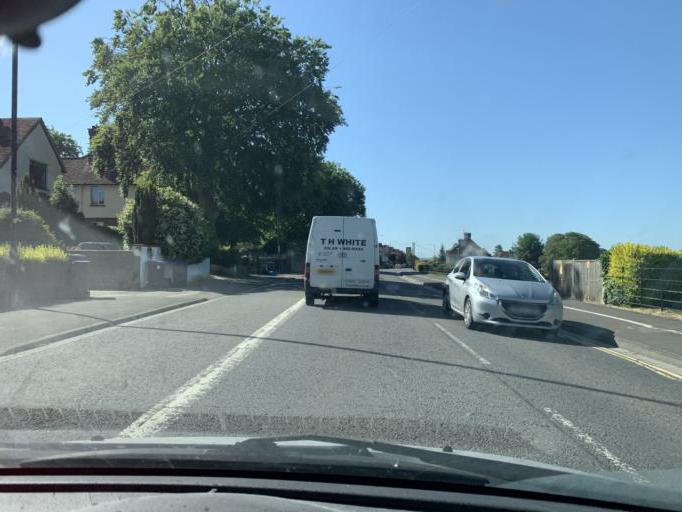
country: GB
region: England
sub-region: Wiltshire
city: Salisbury
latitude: 51.0868
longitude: -1.7981
